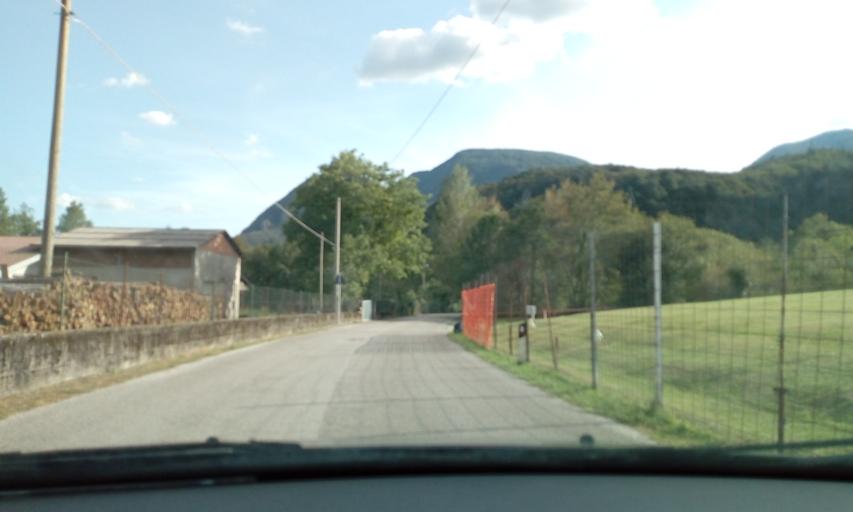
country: IT
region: Friuli Venezia Giulia
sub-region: Provincia di Udine
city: Trasaghis
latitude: 46.3099
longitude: 13.0509
